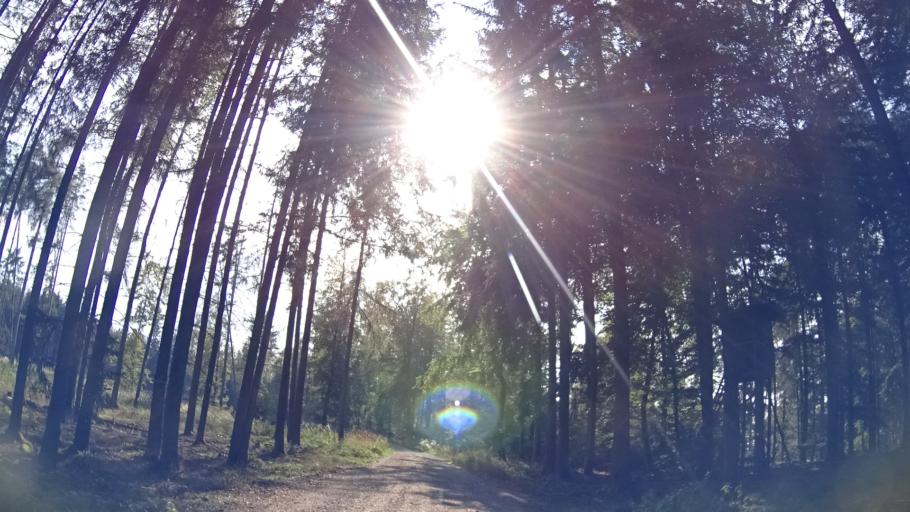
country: DE
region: Bavaria
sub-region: Lower Bavaria
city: Riedenburg
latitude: 48.9781
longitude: 11.6736
